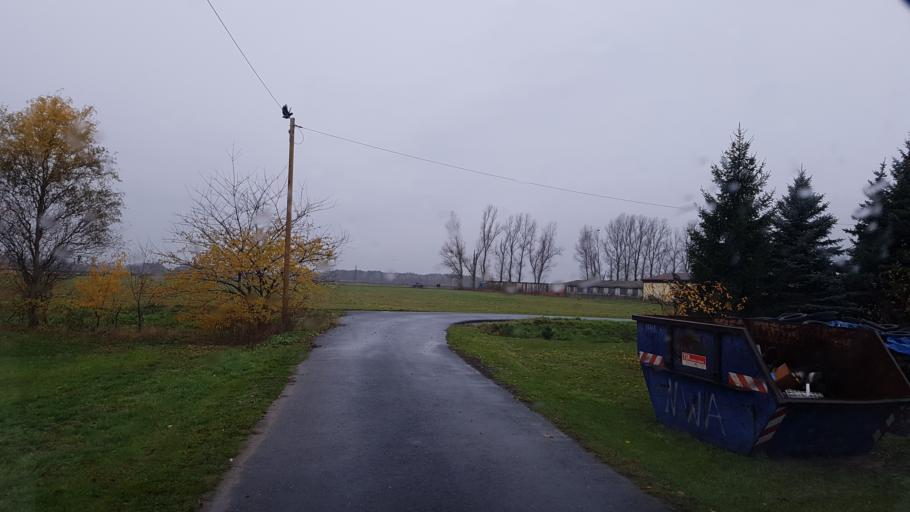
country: DE
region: Brandenburg
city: Herzberg
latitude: 51.6538
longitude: 13.2214
